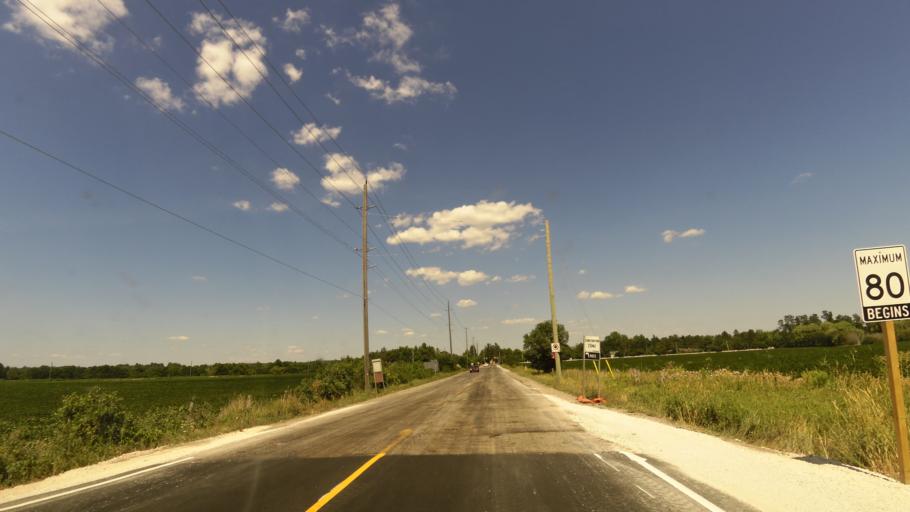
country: CA
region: Ontario
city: Brampton
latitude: 43.6400
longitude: -79.8604
